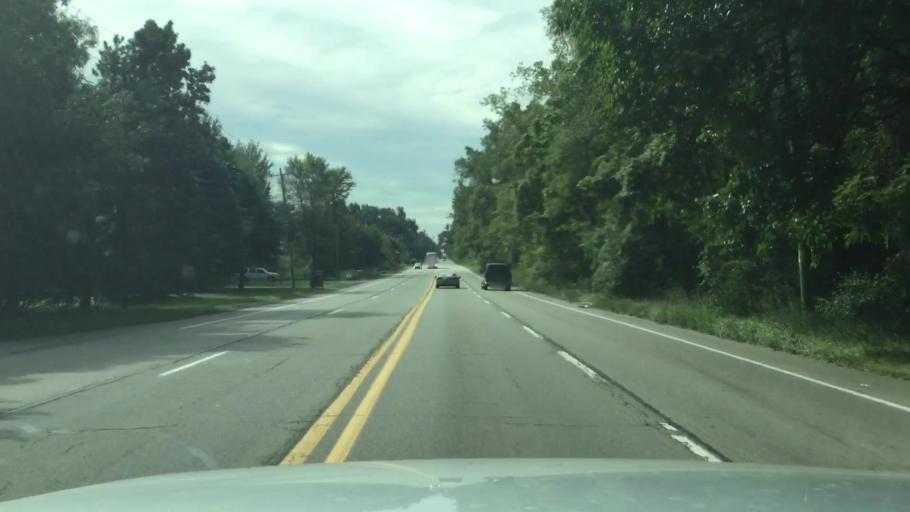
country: US
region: Michigan
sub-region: Wayne County
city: Belleville
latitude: 42.2558
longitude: -83.4866
